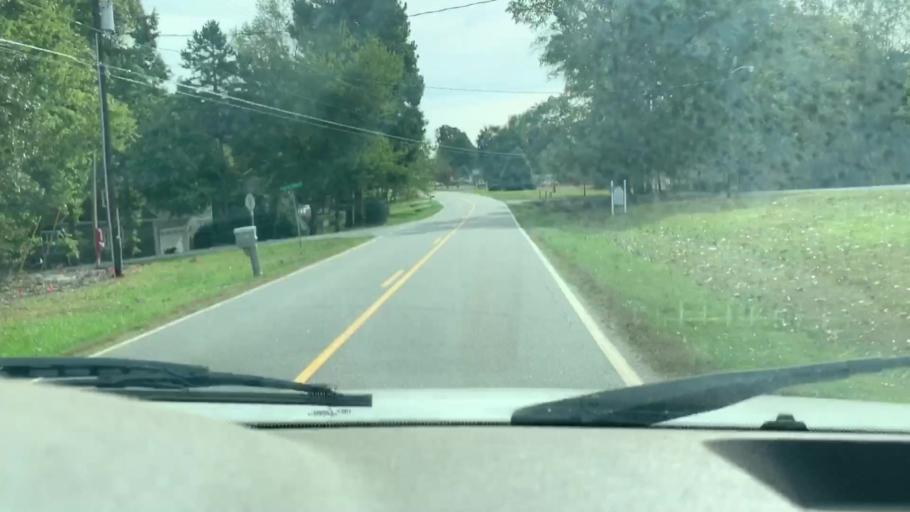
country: US
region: North Carolina
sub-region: Catawba County
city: Lake Norman of Catawba
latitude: 35.5665
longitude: -80.9303
